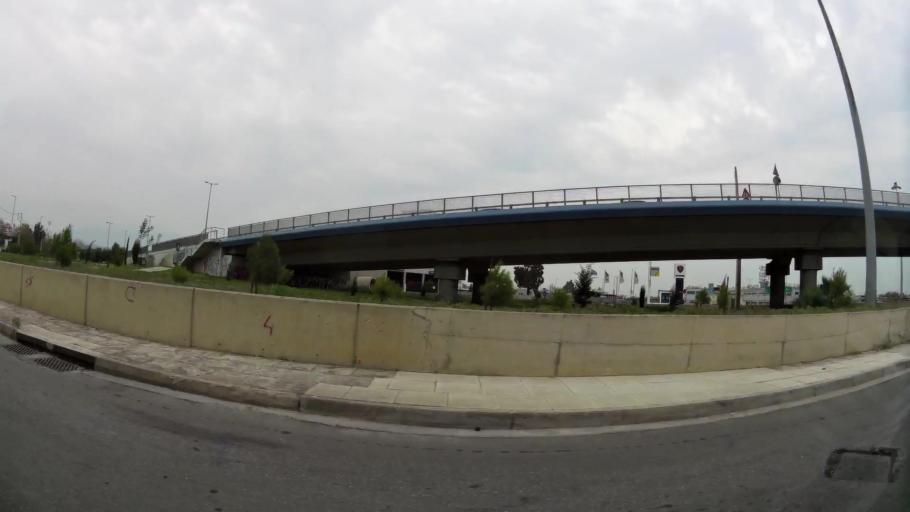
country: GR
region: Attica
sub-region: Nomos Piraios
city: Agios Ioannis Rentis
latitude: 37.9693
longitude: 23.6770
